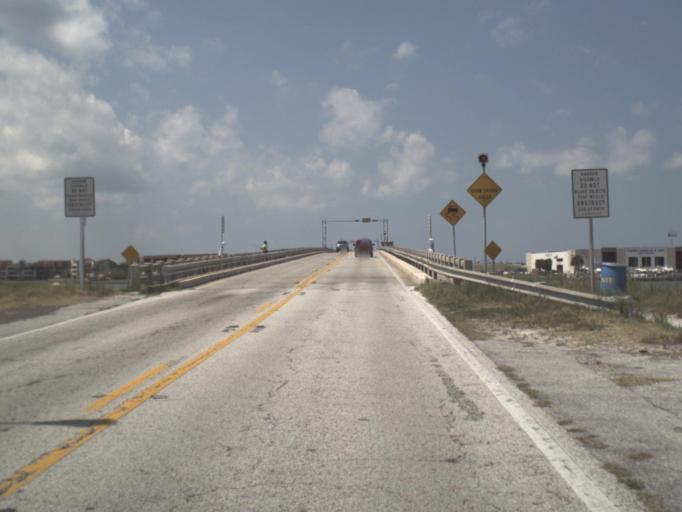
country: US
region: Florida
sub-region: Pinellas County
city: Tierra Verde
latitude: 27.6955
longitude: -82.7167
